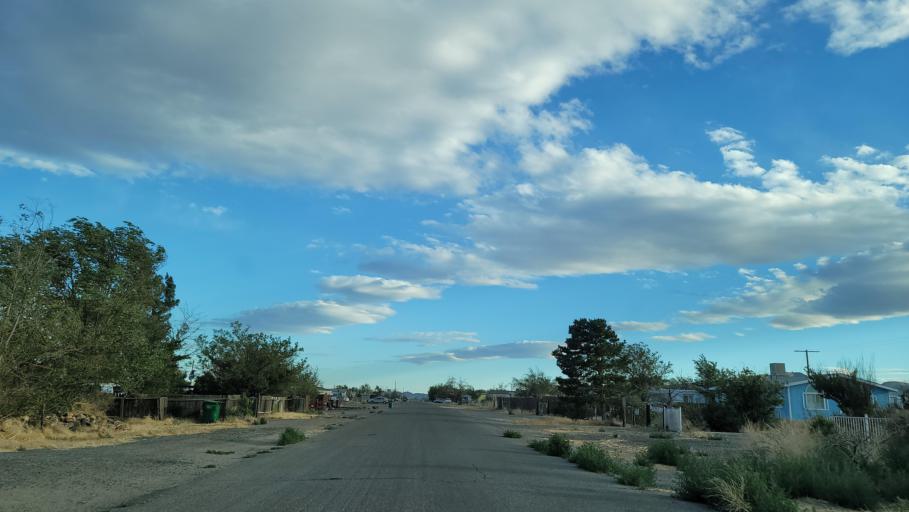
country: US
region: Nevada
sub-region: Lyon County
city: Silver Springs
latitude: 39.4101
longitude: -119.2218
